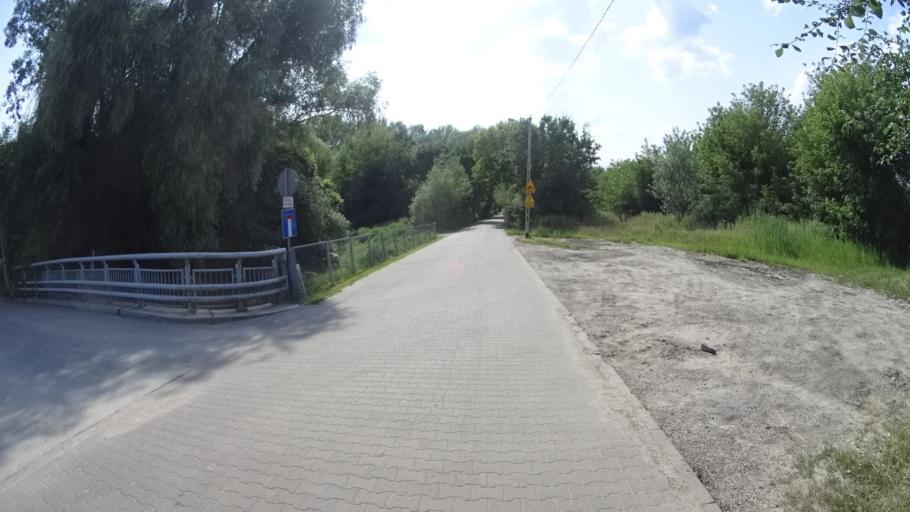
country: PL
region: Masovian Voivodeship
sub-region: Warszawa
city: Ursynow
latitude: 52.1694
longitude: 21.0537
